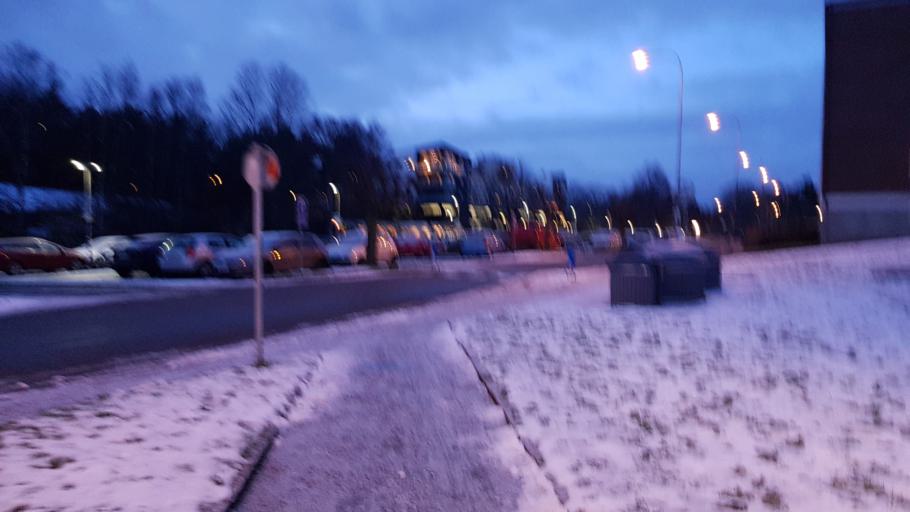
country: SE
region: Vaestra Goetaland
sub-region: Goteborg
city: Majorna
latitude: 57.6659
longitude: 11.9258
